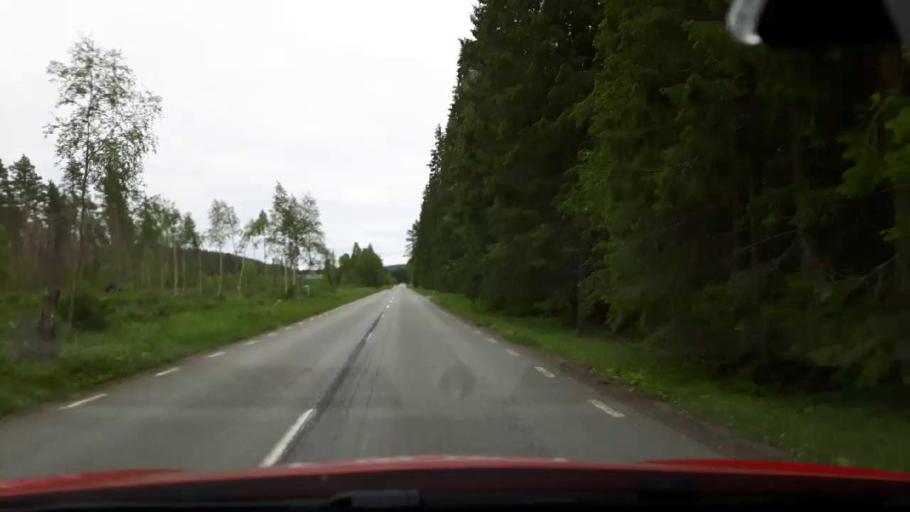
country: SE
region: Jaemtland
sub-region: Stroemsunds Kommun
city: Stroemsund
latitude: 63.4417
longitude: 15.4821
